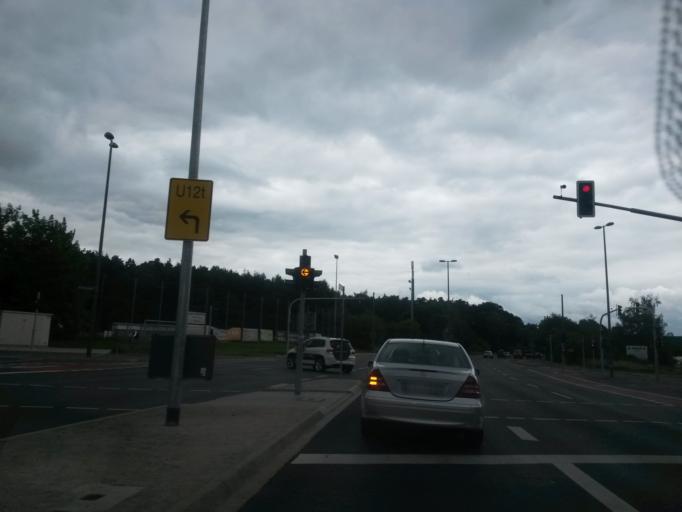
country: DE
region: Bavaria
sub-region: Regierungsbezirk Mittelfranken
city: Zirndorf
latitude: 49.4674
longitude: 10.9539
